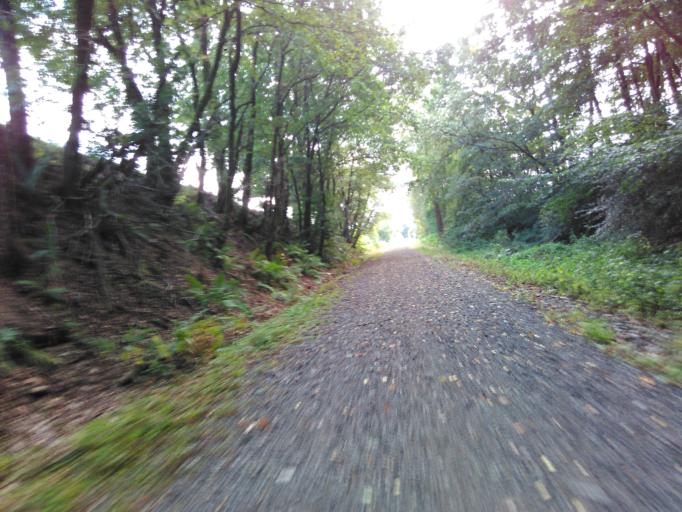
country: BE
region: Wallonia
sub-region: Province du Luxembourg
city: Neufchateau
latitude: 49.9126
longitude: 5.4377
